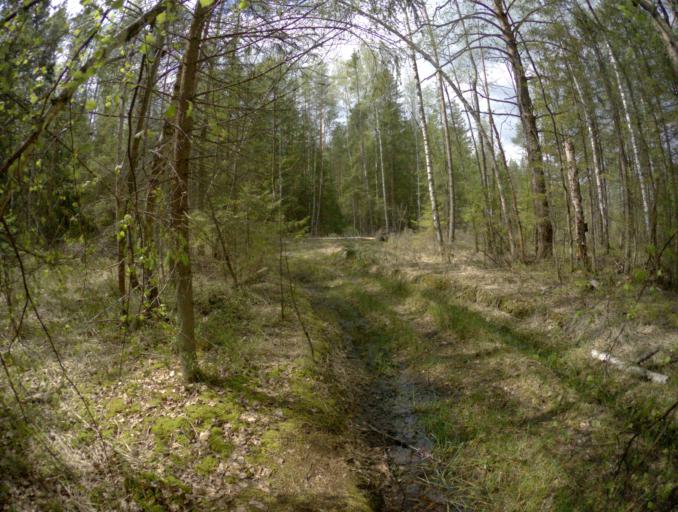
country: RU
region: Vladimir
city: Golovino
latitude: 55.9290
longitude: 40.3861
